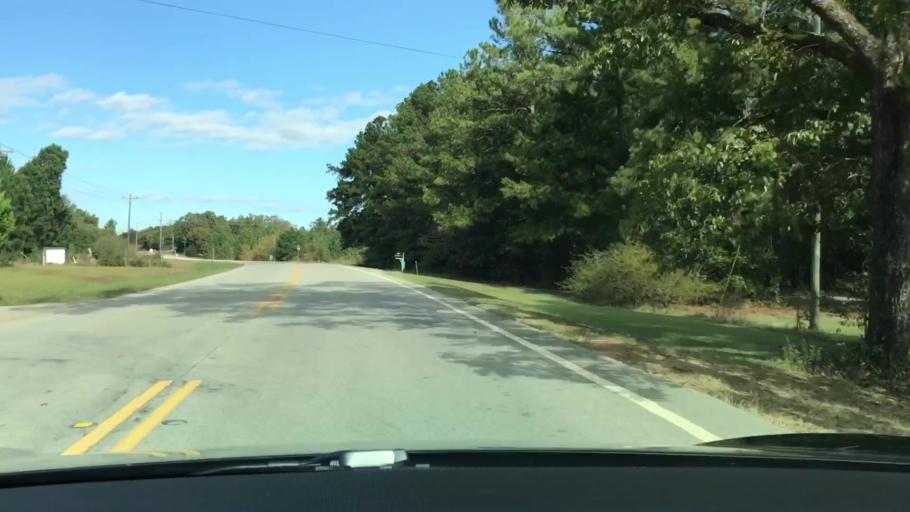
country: US
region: Georgia
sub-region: Jefferson County
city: Wrens
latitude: 33.1867
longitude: -82.4552
